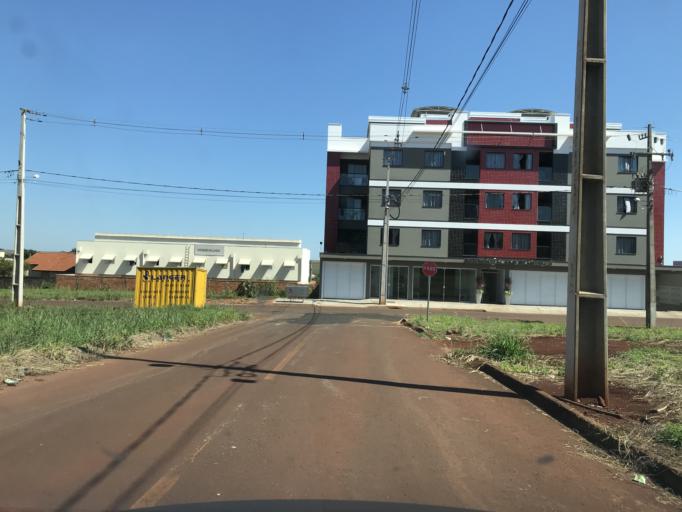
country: BR
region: Parana
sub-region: Palotina
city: Palotina
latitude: -24.2966
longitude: -53.8445
